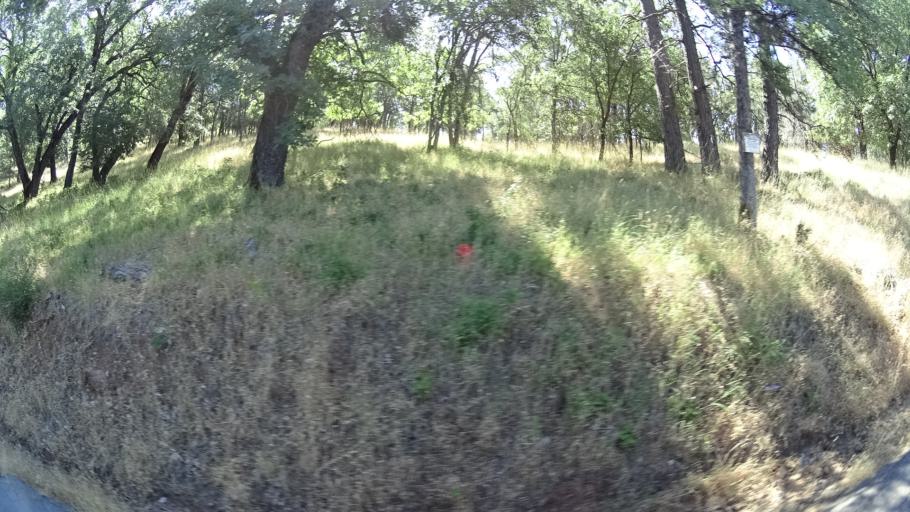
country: US
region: California
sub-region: Amador County
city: Pioneer
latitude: 38.3950
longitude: -120.4753
